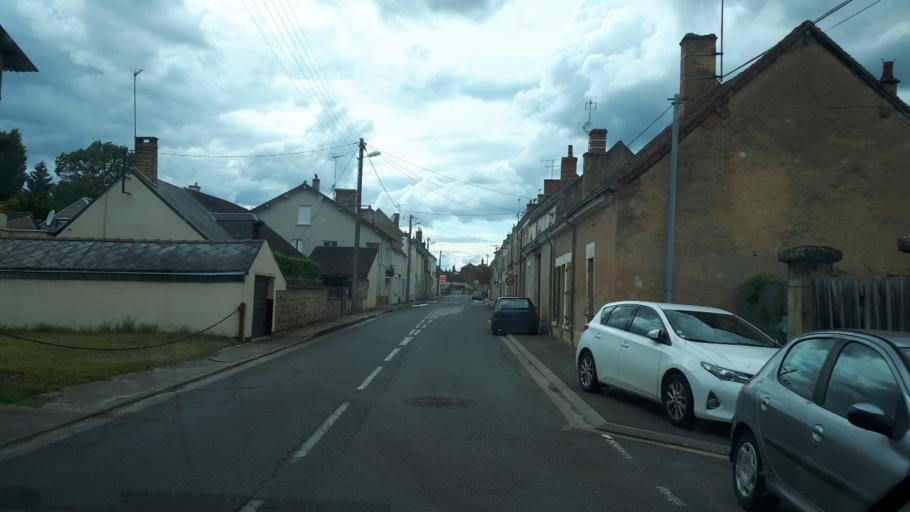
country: FR
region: Centre
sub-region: Departement du Cher
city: Gracay
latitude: 47.1434
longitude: 1.8505
